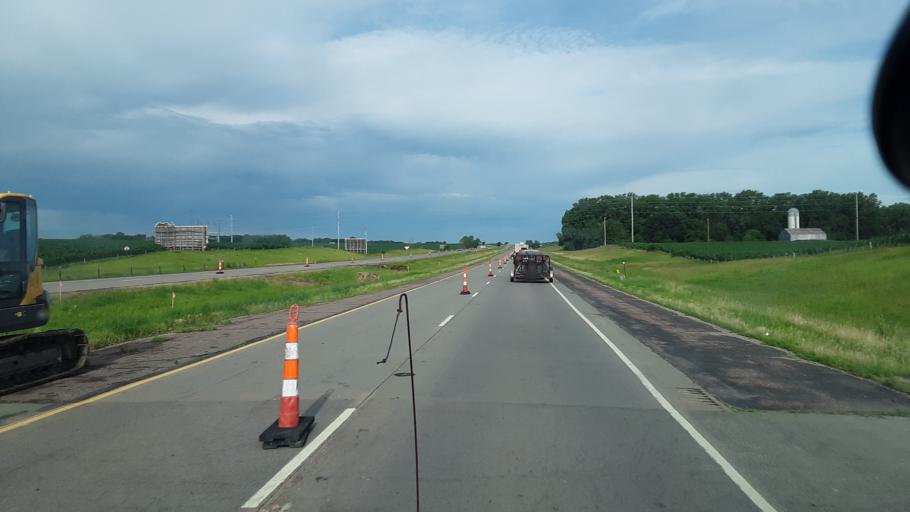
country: US
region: South Dakota
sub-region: Minnehaha County
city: Crooks
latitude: 43.6088
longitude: -96.8274
